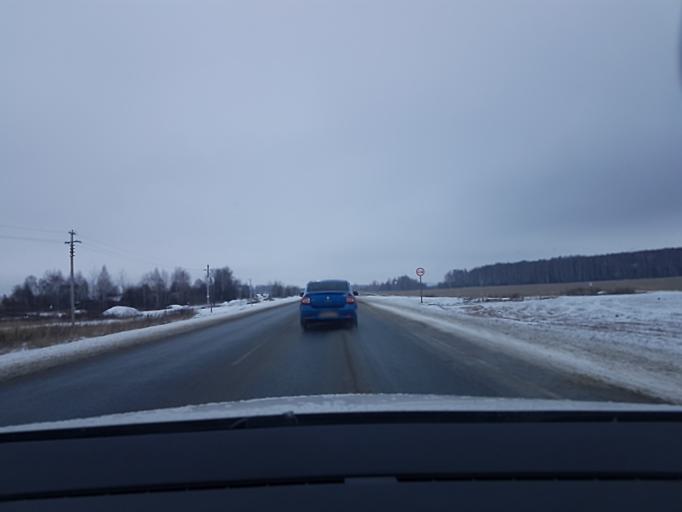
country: RU
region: Moskovskaya
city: Ozherel'ye
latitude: 54.6421
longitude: 38.3693
